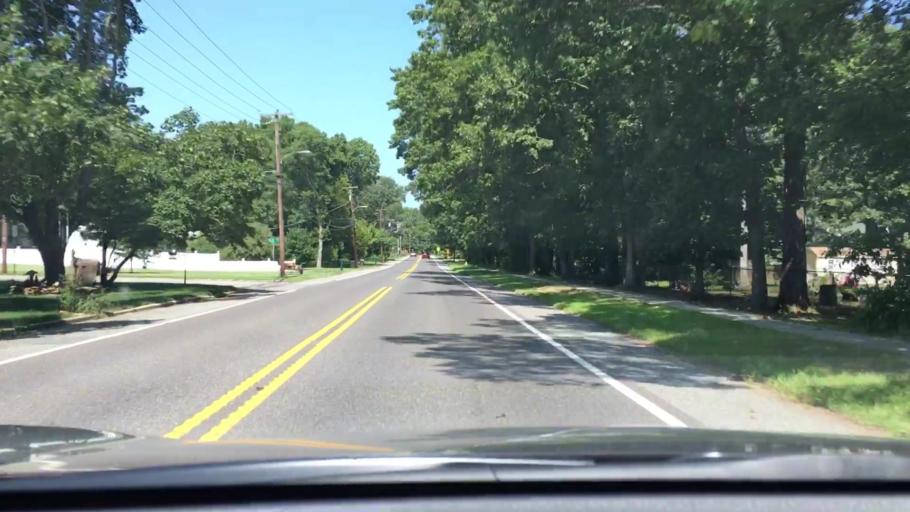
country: US
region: New Jersey
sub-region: Cumberland County
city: Millville
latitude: 39.3843
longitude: -75.0724
